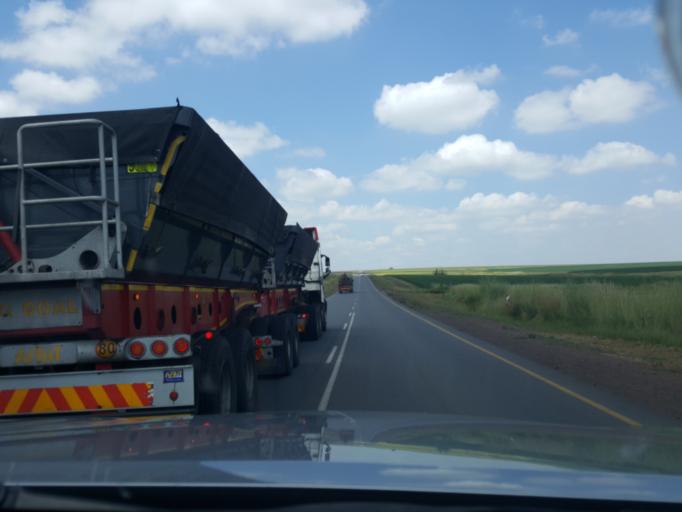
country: ZA
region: Mpumalanga
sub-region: Nkangala District Municipality
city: Middelburg
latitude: -26.0258
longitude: 29.4365
